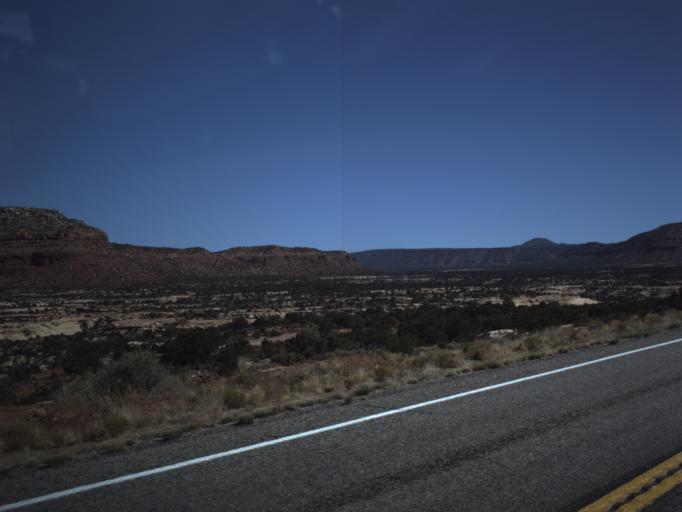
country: US
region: Utah
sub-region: San Juan County
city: Blanding
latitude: 37.6552
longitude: -110.1363
